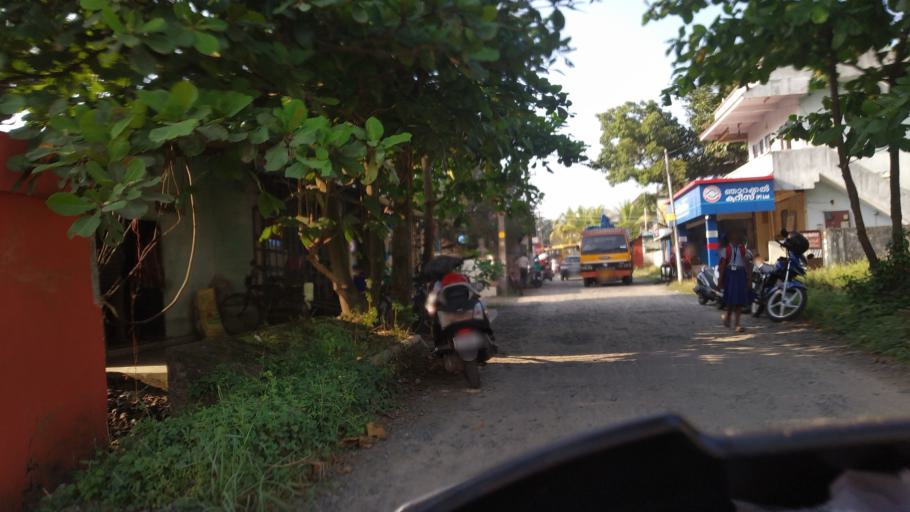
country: IN
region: Kerala
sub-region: Ernakulam
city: Elur
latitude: 10.0469
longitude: 76.2203
